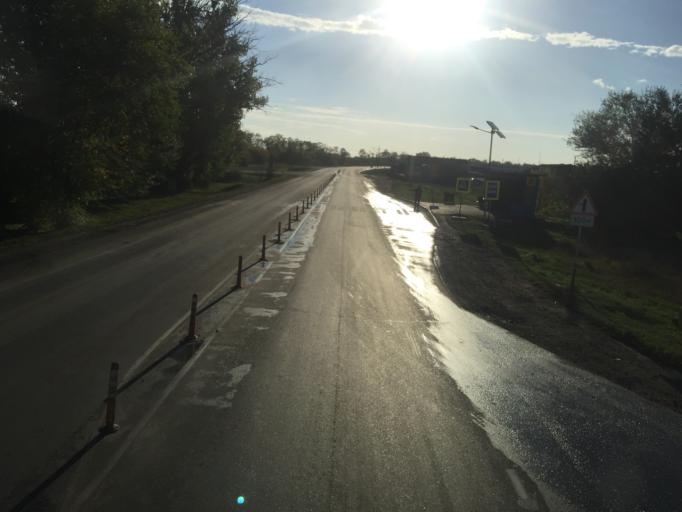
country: RU
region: Rostov
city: Mechetinskaya
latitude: 46.7577
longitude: 40.4499
